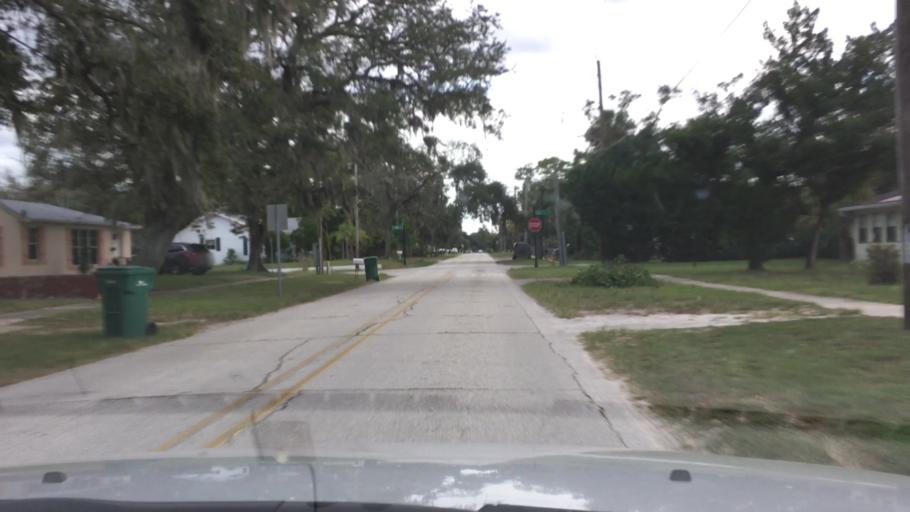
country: US
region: Florida
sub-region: Volusia County
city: Holly Hill
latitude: 29.2328
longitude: -81.0321
